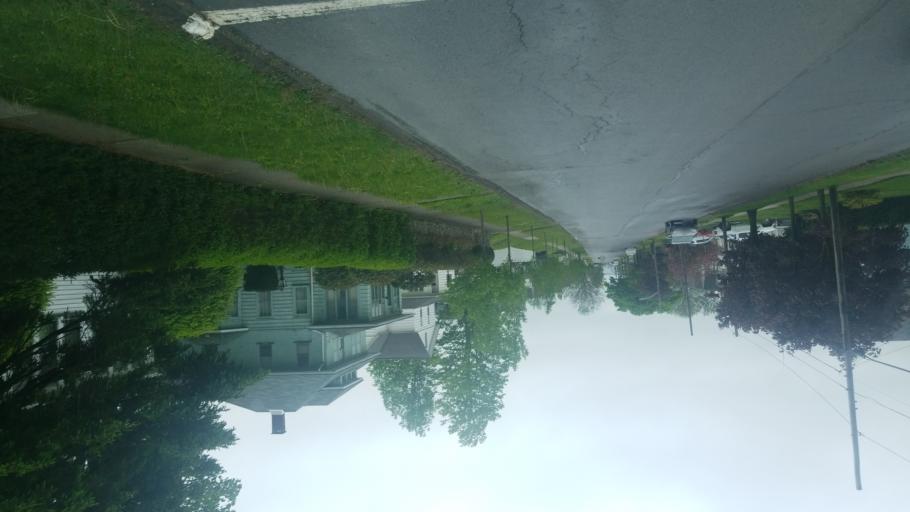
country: US
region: Pennsylvania
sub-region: McKean County
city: Kane
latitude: 41.6559
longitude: -78.8053
